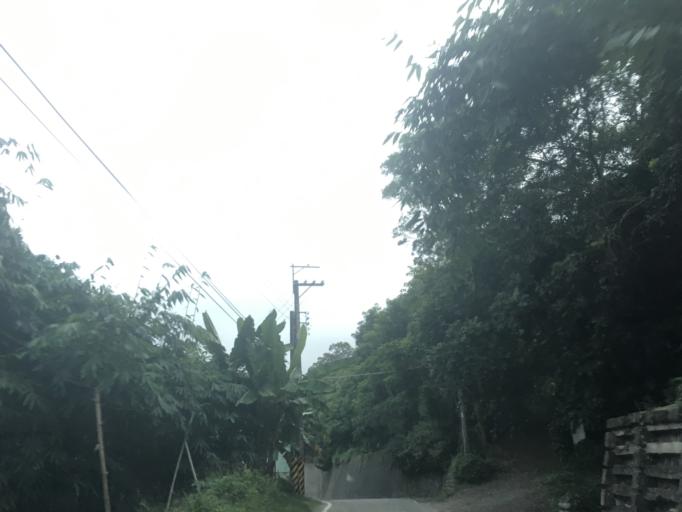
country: TW
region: Taiwan
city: Fengyuan
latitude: 24.1903
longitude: 120.7482
